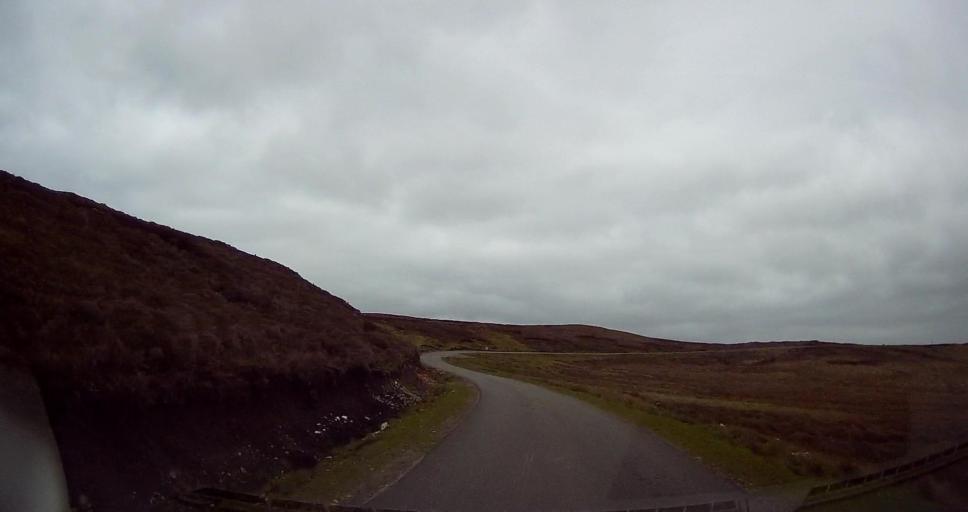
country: GB
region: Scotland
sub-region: Shetland Islands
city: Lerwick
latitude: 60.3172
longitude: -1.3413
